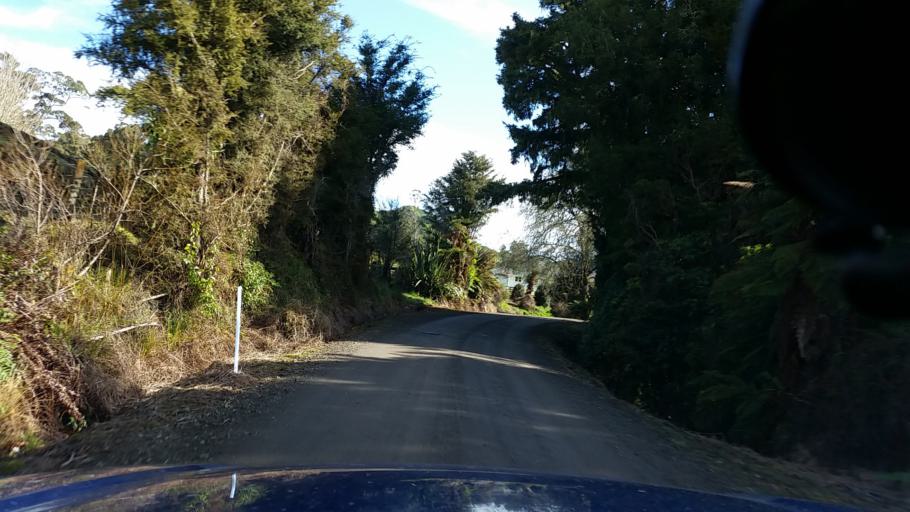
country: NZ
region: Taranaki
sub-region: New Plymouth District
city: Waitara
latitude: -39.0599
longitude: 174.7827
